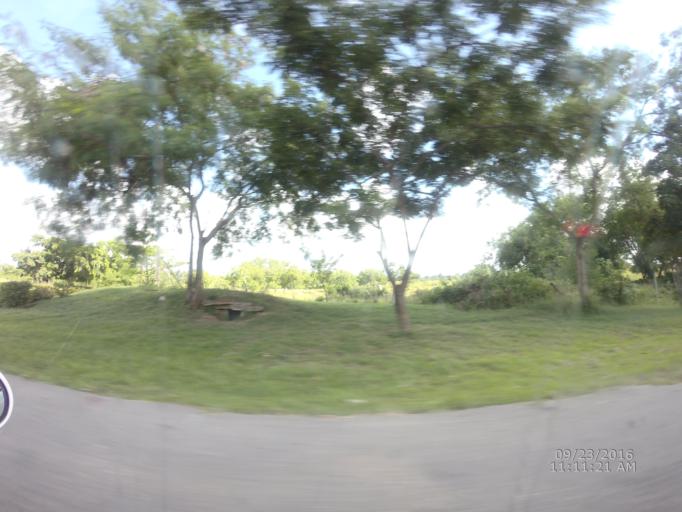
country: CU
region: La Habana
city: Arroyo Naranjo
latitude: 23.0250
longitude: -82.2682
